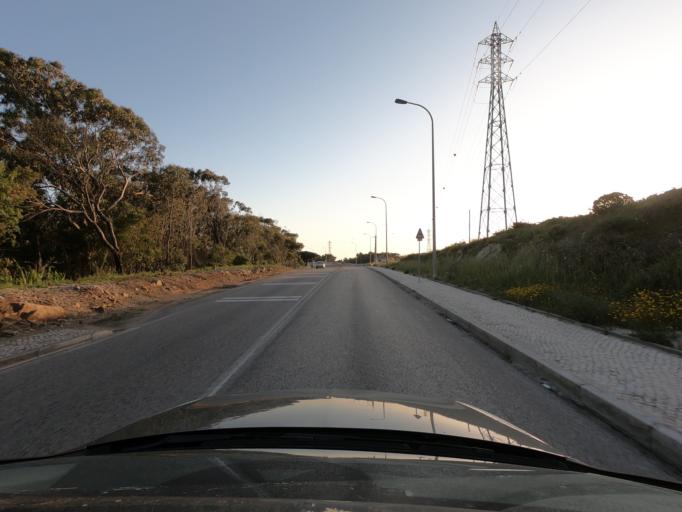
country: PT
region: Lisbon
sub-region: Cascais
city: Alcabideche
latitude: 38.7570
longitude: -9.3848
